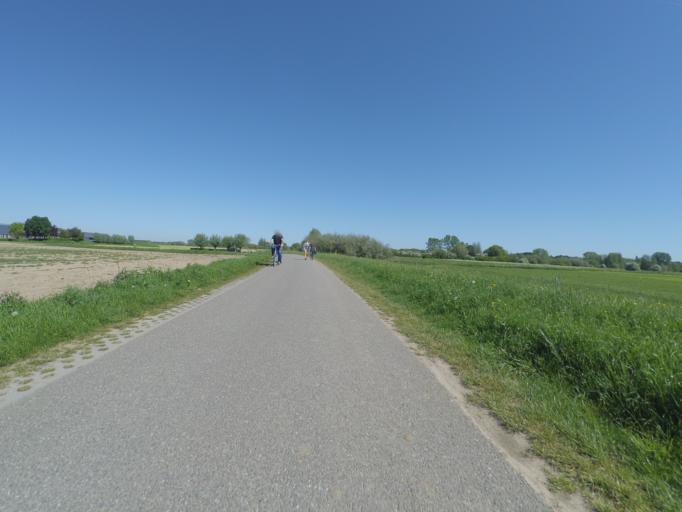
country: NL
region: Gelderland
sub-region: Gemeente Lochem
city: Epse
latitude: 52.2126
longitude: 6.1808
